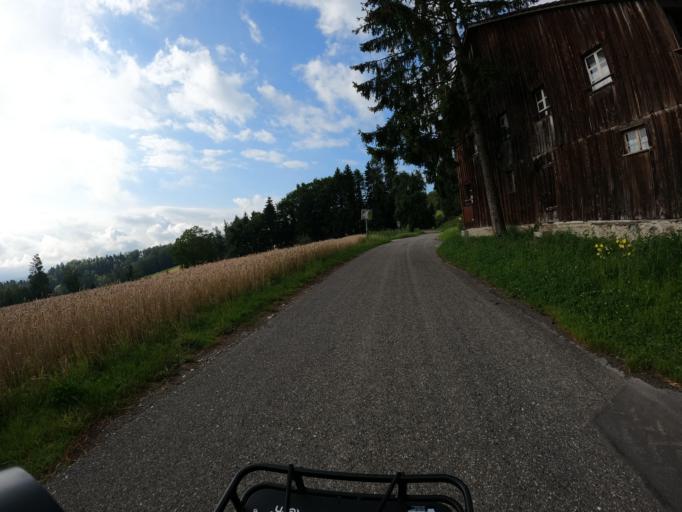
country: CH
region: Aargau
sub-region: Bezirk Muri
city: Buttwil
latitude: 47.2415
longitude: 8.3260
